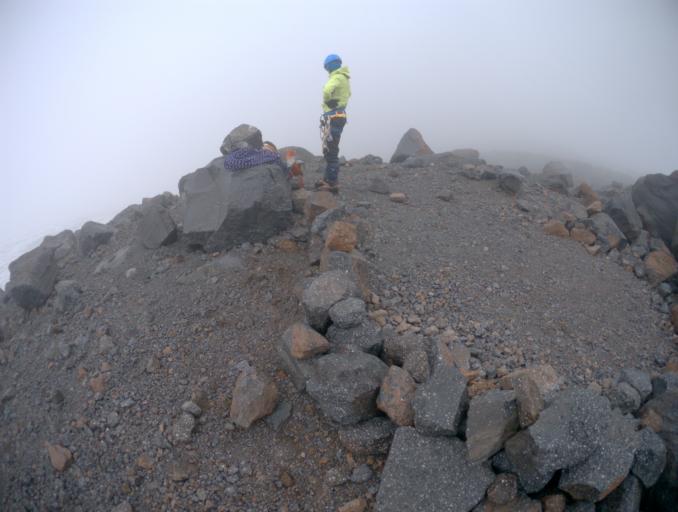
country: RU
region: Kabardino-Balkariya
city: Terskol
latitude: 43.3711
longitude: 42.4957
